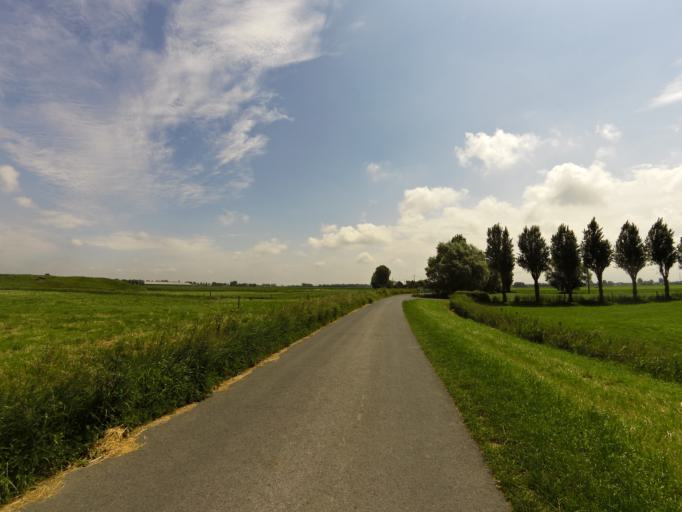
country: BE
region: Flanders
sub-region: Provincie West-Vlaanderen
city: Nieuwpoort
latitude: 51.1426
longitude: 2.7948
